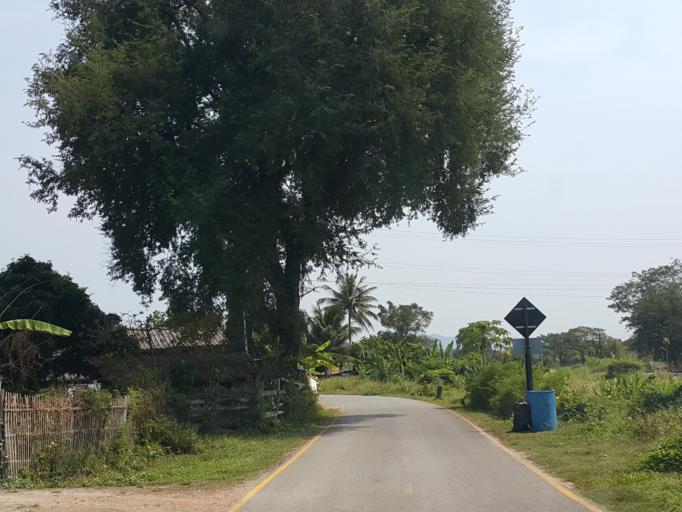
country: TH
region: Lampang
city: Lampang
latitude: 18.3037
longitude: 99.4290
